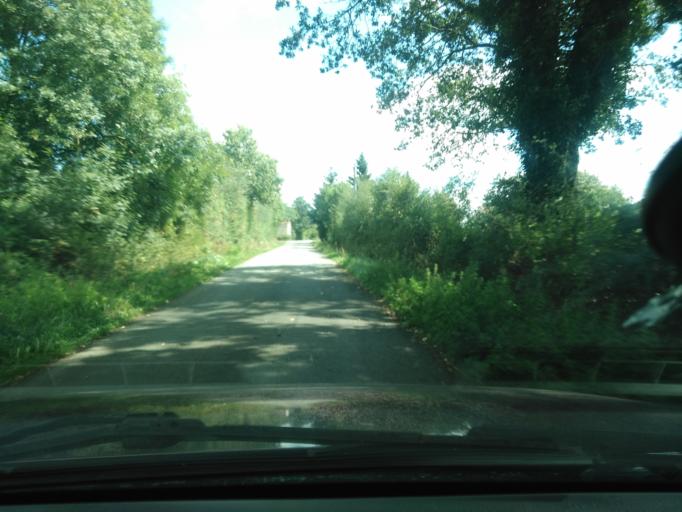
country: FR
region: Pays de la Loire
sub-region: Departement de la Vendee
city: Dompierre-sur-Yon
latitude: 46.7425
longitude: -1.3570
